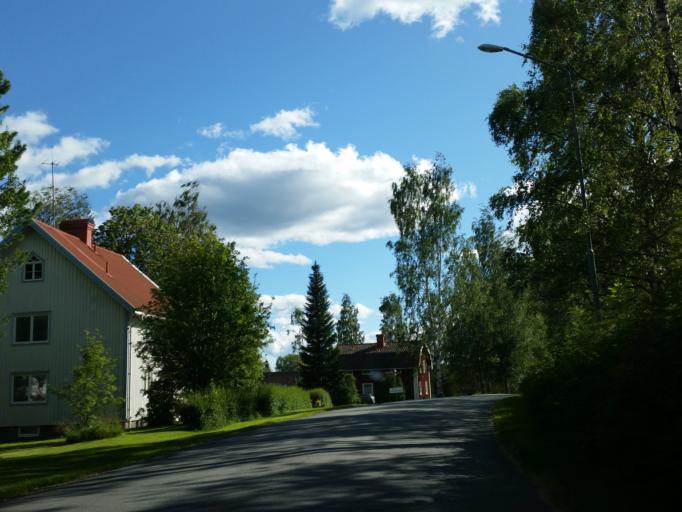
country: SE
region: Vaesterbotten
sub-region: Robertsfors Kommun
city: Robertsfors
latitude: 64.1874
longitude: 20.8554
